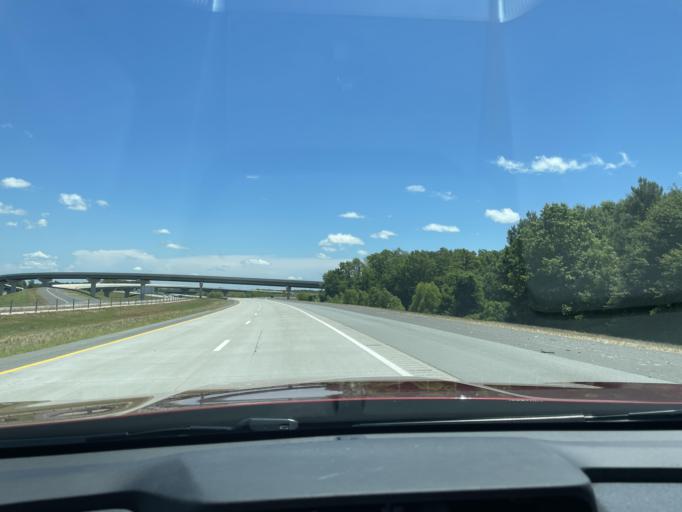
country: US
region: Arkansas
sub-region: Jefferson County
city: Pine Bluff
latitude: 34.1719
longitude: -91.9950
